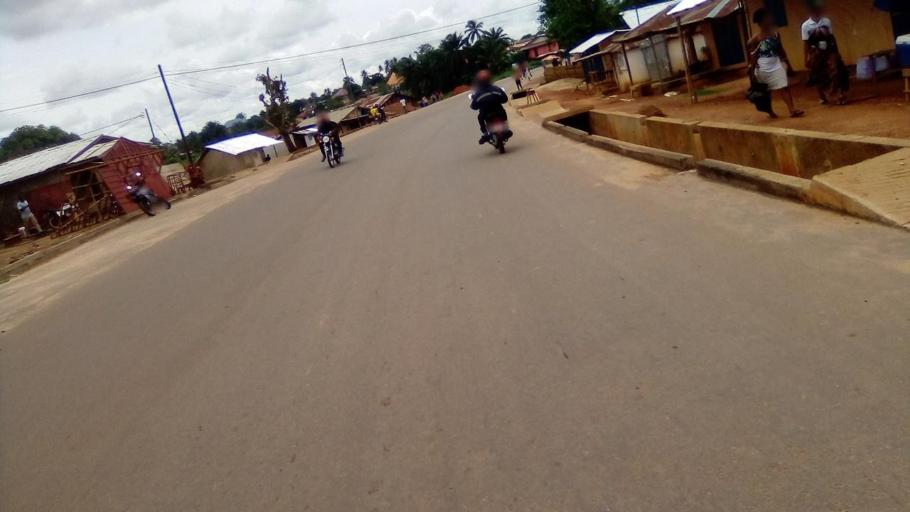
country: SL
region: Southern Province
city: Bo
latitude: 7.9506
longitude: -11.7569
